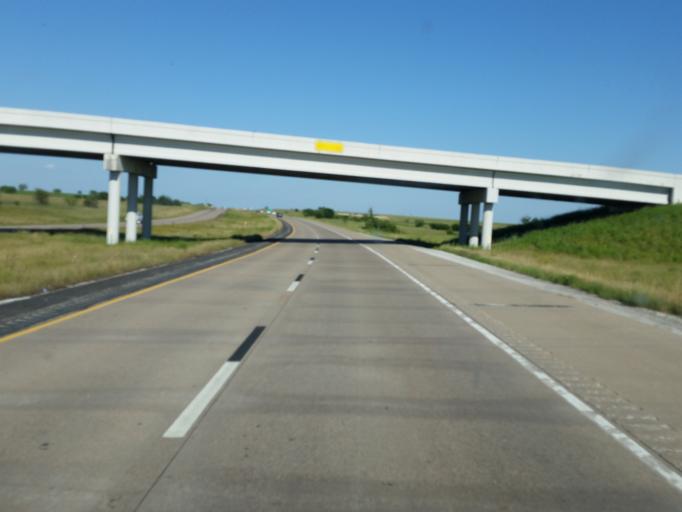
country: US
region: Texas
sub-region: Parker County
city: Aledo
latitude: 32.6966
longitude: -97.5382
